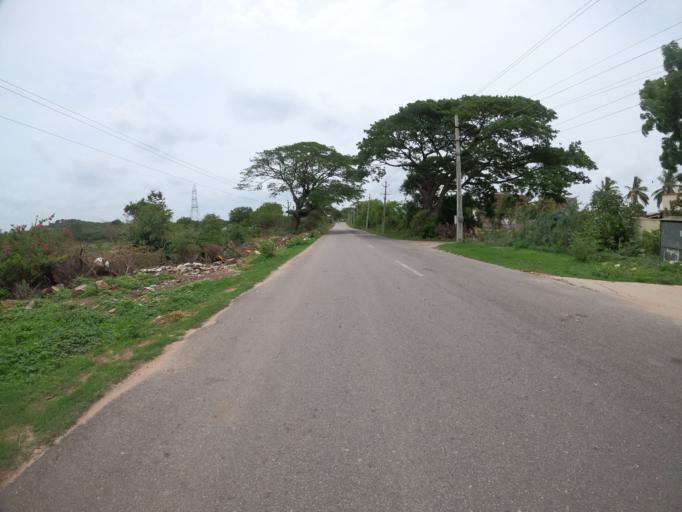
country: IN
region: Telangana
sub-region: Hyderabad
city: Hyderabad
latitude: 17.3430
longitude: 78.3608
